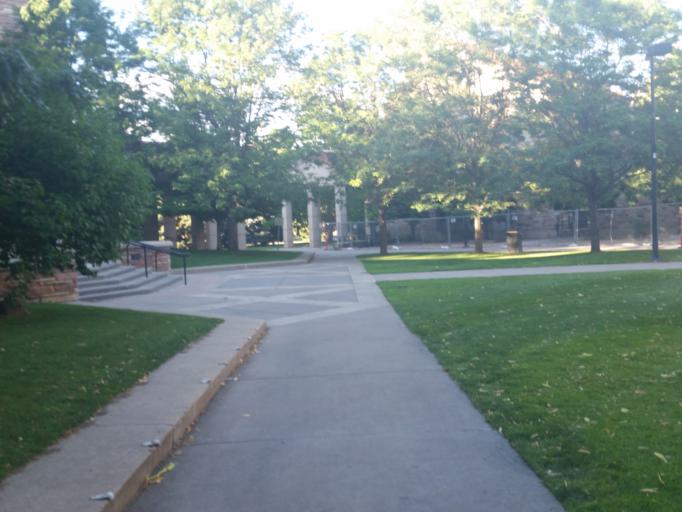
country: US
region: Colorado
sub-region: Boulder County
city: Boulder
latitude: 40.0073
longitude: -105.2644
